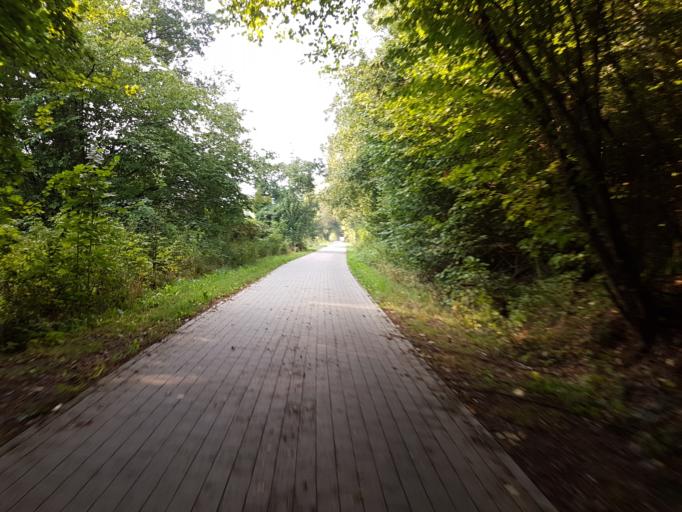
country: DE
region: Saxony
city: Wittgensdorf
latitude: 50.8844
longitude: 12.8916
